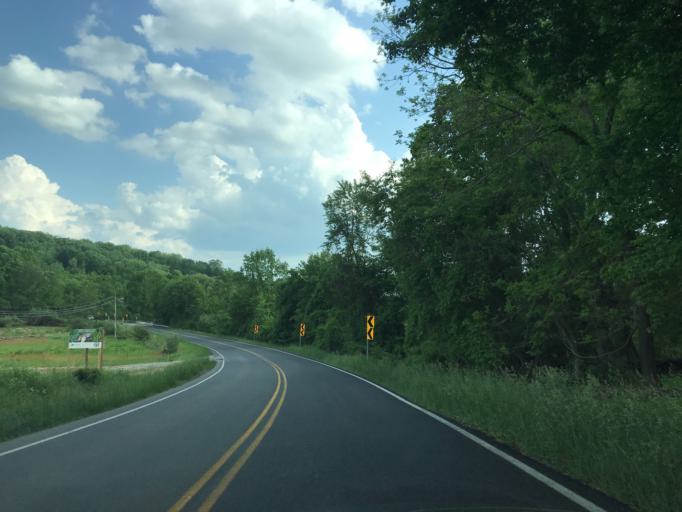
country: US
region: Maryland
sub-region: Harford County
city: Bel Air North
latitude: 39.5468
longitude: -76.3931
